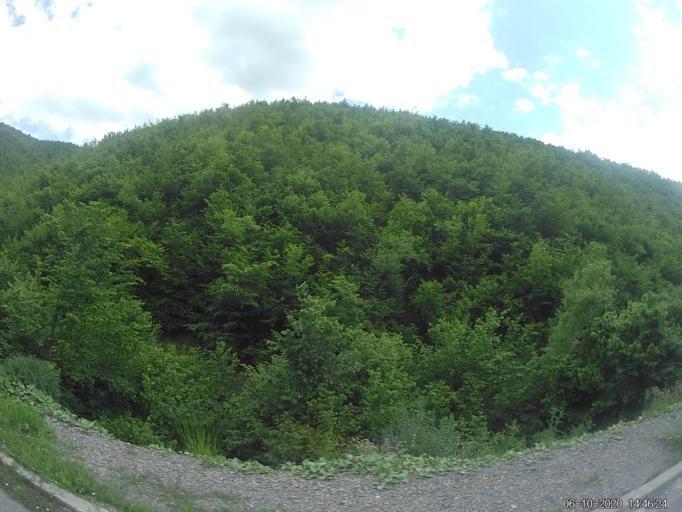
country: XK
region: Prizren
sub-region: Komuna e Therandes
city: Budakovo
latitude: 42.3837
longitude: 20.9572
